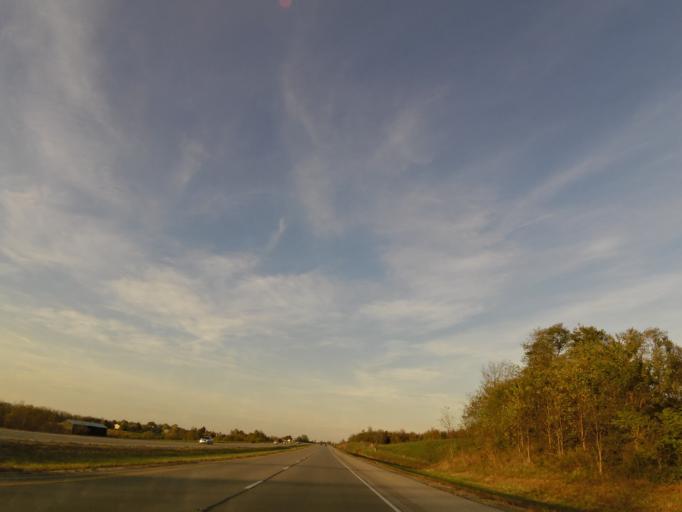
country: US
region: Kentucky
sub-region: Garrard County
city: Lancaster
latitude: 37.7162
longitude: -84.6451
